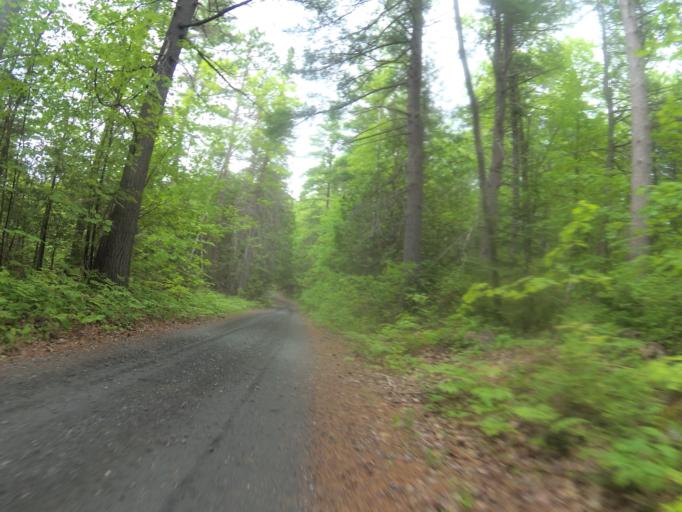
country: CA
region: Ontario
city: Renfrew
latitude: 45.1033
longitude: -76.8284
